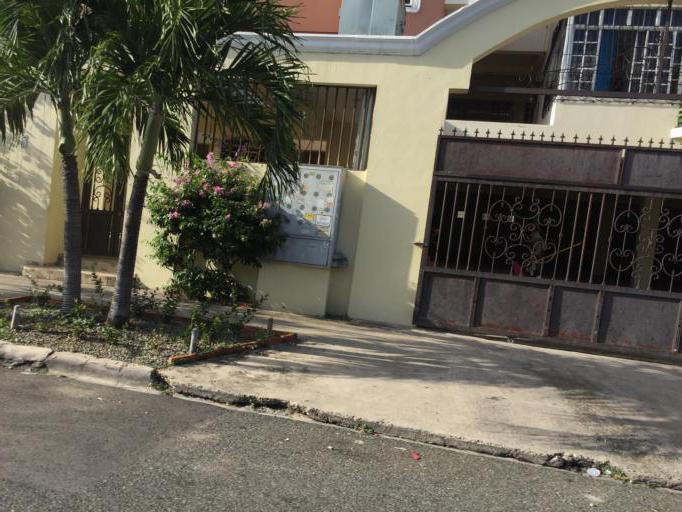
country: DO
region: Nacional
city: La Julia
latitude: 18.4619
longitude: -69.9204
